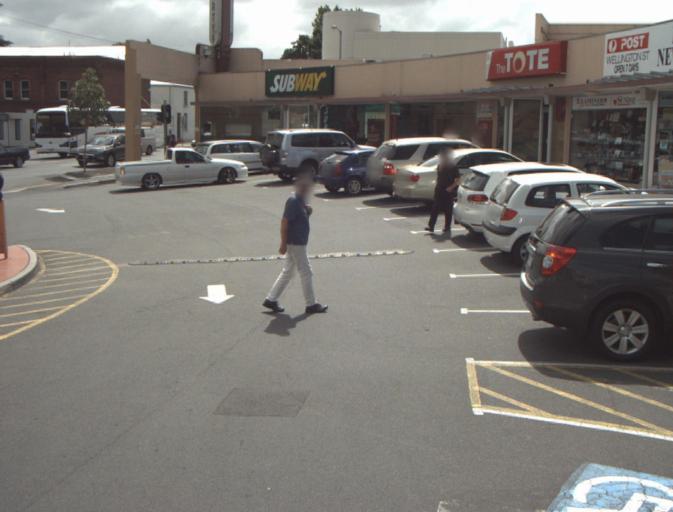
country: AU
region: Tasmania
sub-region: Launceston
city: Launceston
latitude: -41.4393
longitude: 147.1365
